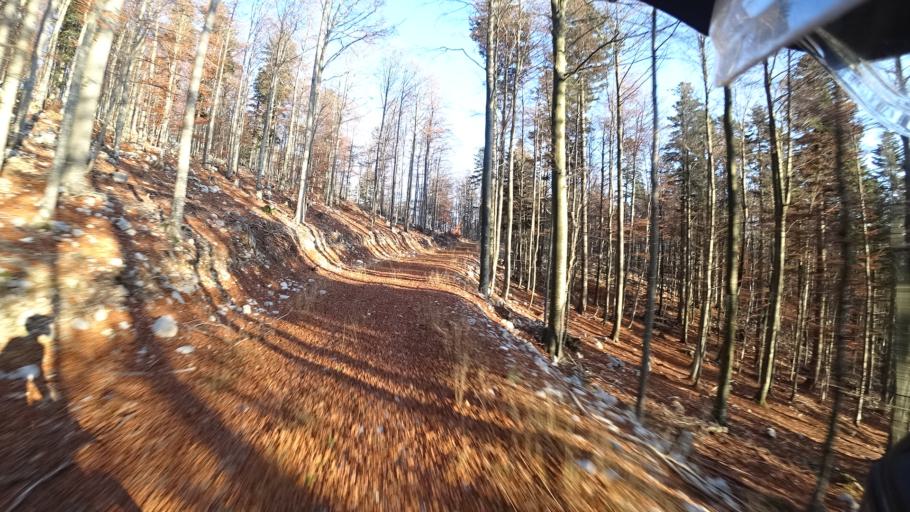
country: HR
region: Primorsko-Goranska
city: Drazice
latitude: 45.4830
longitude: 14.4854
